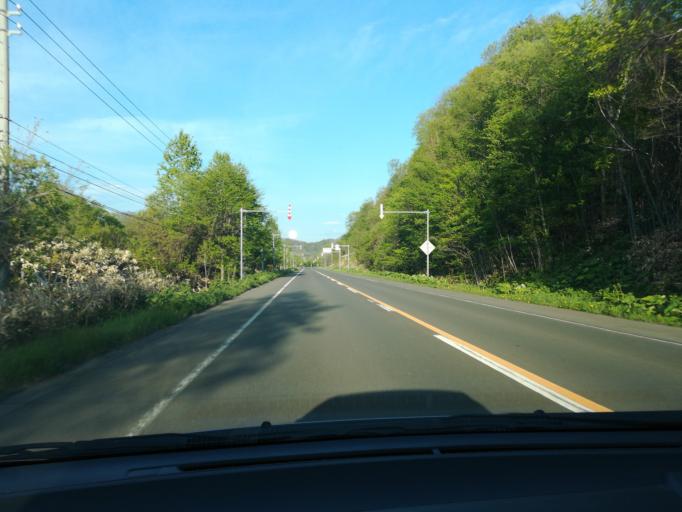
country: JP
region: Hokkaido
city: Shimo-furano
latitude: 43.1360
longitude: 142.6379
